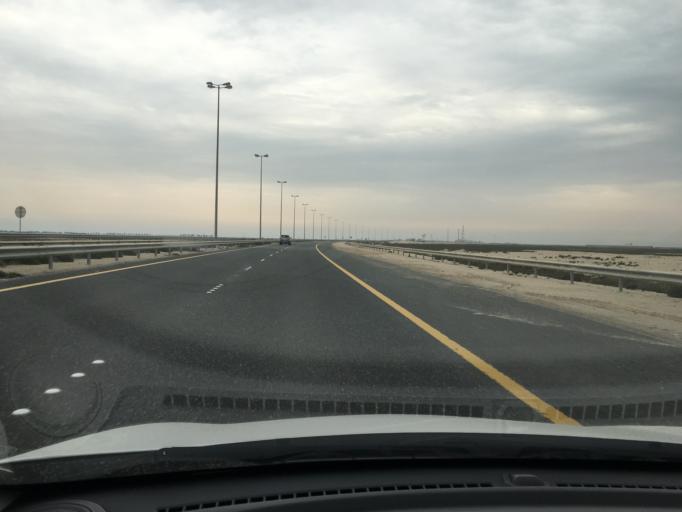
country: BH
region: Central Governorate
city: Dar Kulayb
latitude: 25.8647
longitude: 50.5842
